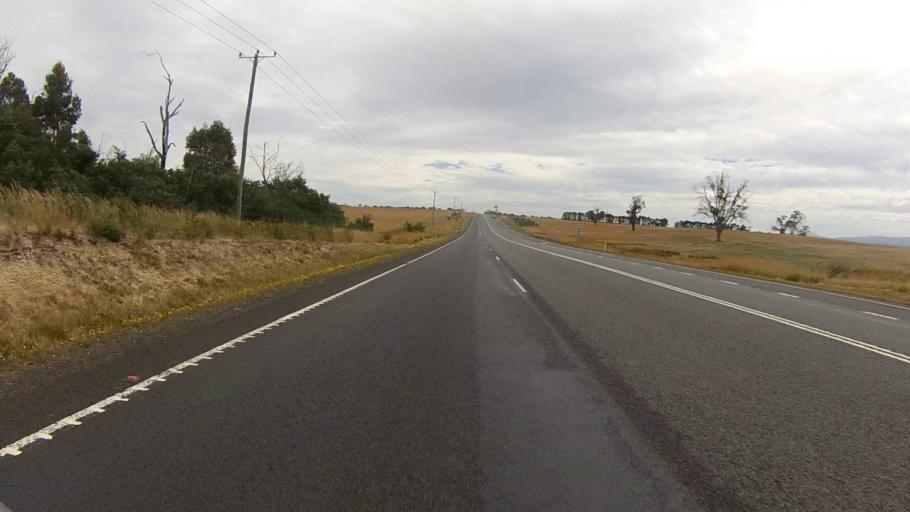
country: AU
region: Tasmania
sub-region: Northern Midlands
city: Evandale
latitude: -41.7182
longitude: 147.3093
